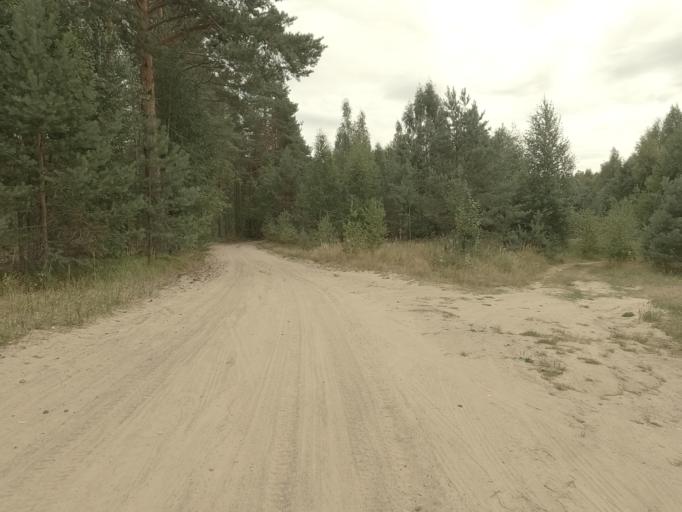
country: RU
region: Leningrad
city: Kamennogorsk
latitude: 60.9997
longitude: 29.1819
